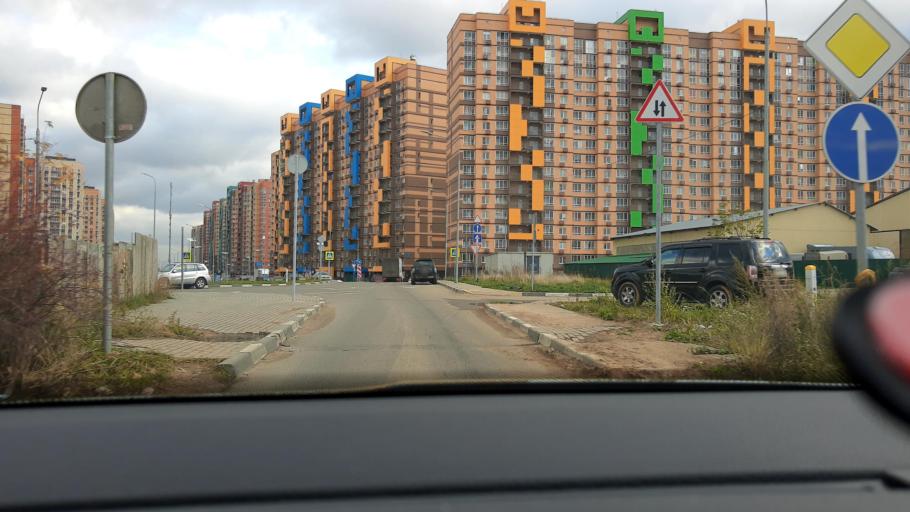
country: RU
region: Moskovskaya
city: Petrovskaya
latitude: 55.5602
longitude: 37.8072
